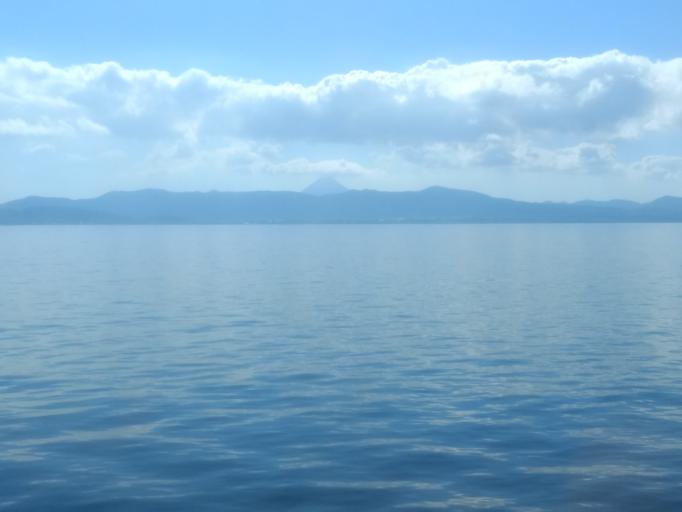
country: JP
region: Kagoshima
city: Ibusuki
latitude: 31.3255
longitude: 130.6831
